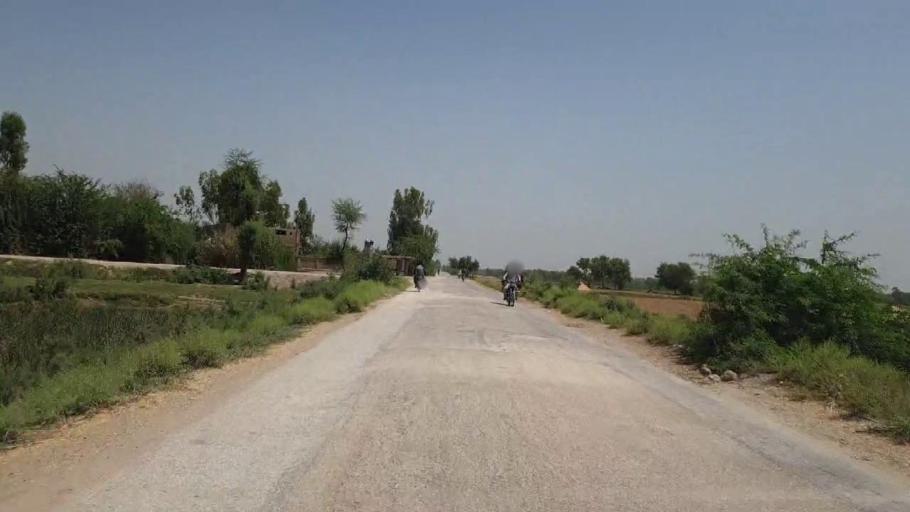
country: PK
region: Sindh
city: Adilpur
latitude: 27.9018
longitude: 69.2939
